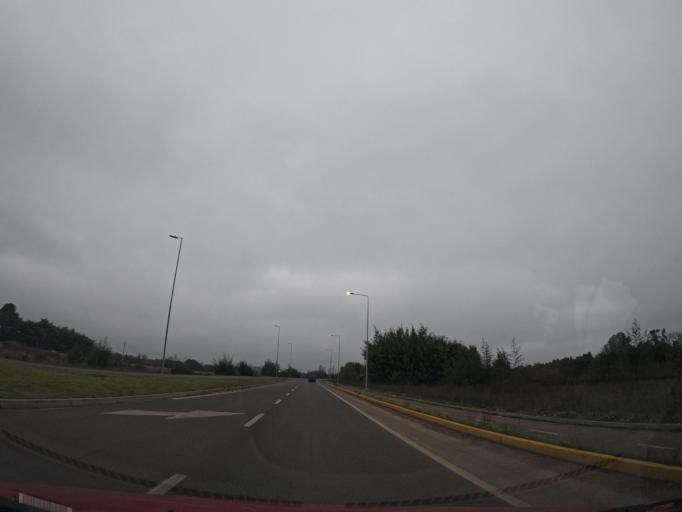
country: CL
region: Maule
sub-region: Provincia de Talca
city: San Clemente
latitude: -35.5279
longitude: -71.4780
